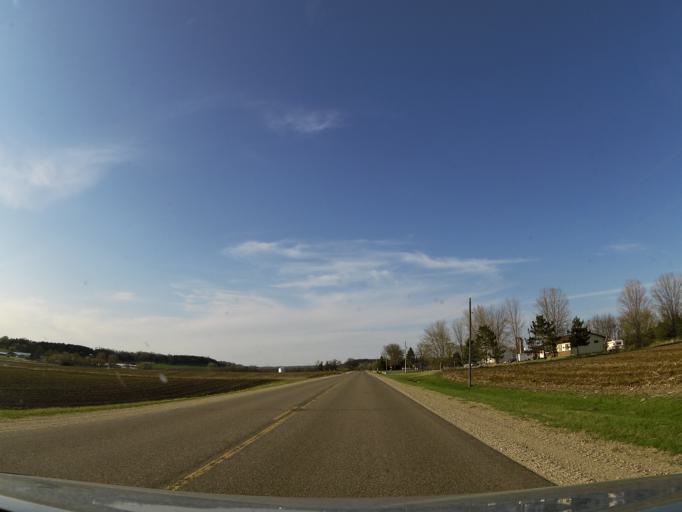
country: US
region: Wisconsin
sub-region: Pierce County
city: River Falls
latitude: 44.8132
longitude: -92.6448
